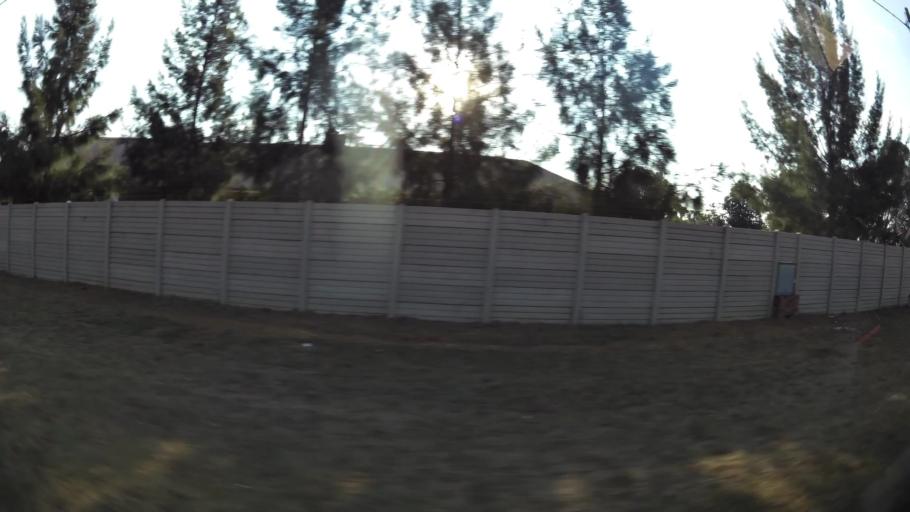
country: ZA
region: Gauteng
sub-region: Ekurhuleni Metropolitan Municipality
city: Benoni
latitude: -26.1398
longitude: 28.3648
